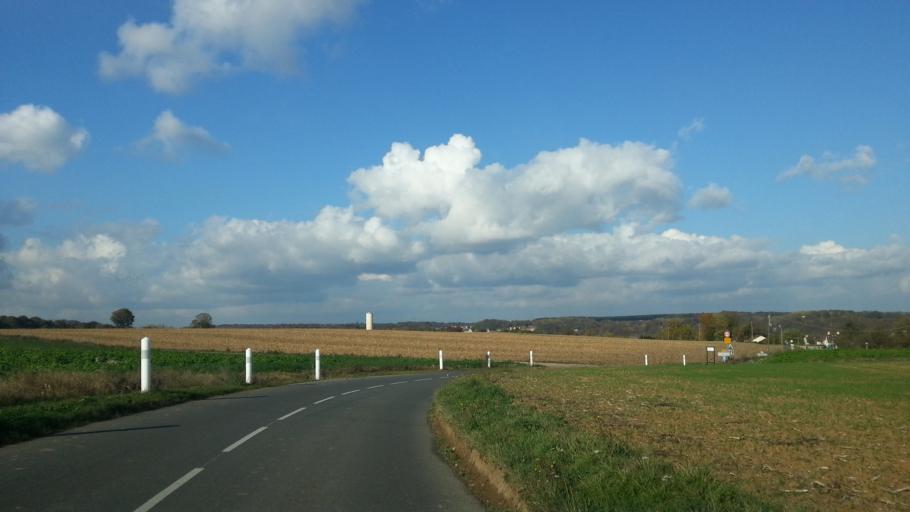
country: FR
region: Picardie
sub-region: Departement de l'Oise
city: Thiverny
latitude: 49.2481
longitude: 2.4034
